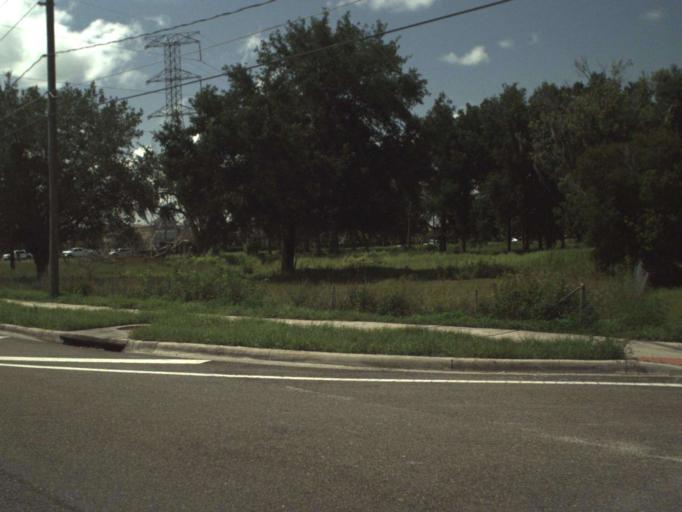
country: US
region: Florida
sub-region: Orange County
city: Conway
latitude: 28.4801
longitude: -81.2894
